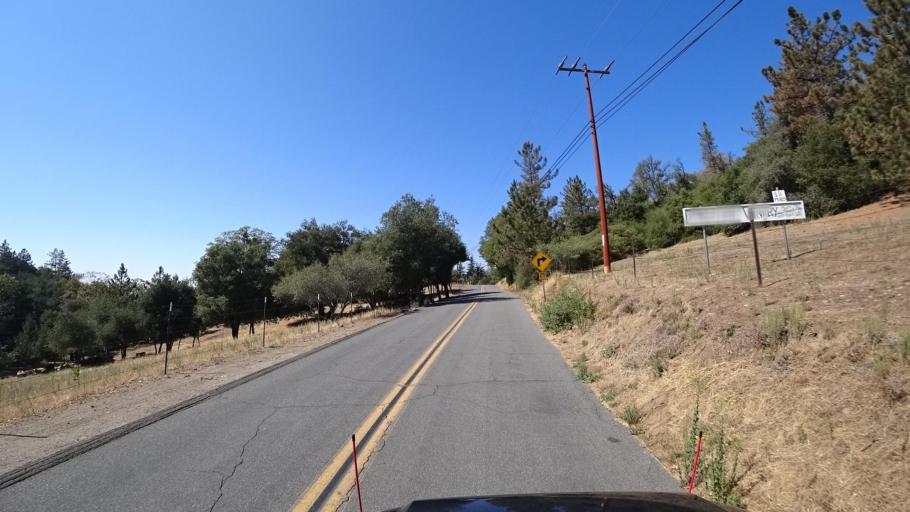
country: US
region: California
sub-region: San Diego County
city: Julian
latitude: 33.0847
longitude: -116.6099
